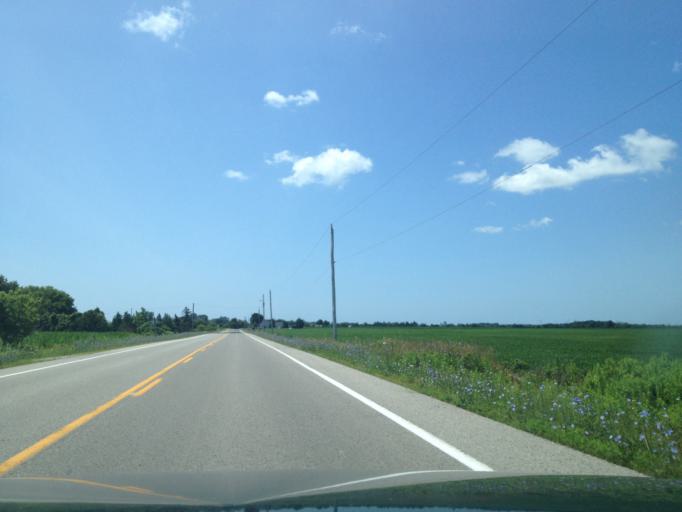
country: CA
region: Ontario
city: Norfolk County
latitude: 42.6115
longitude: -80.4657
